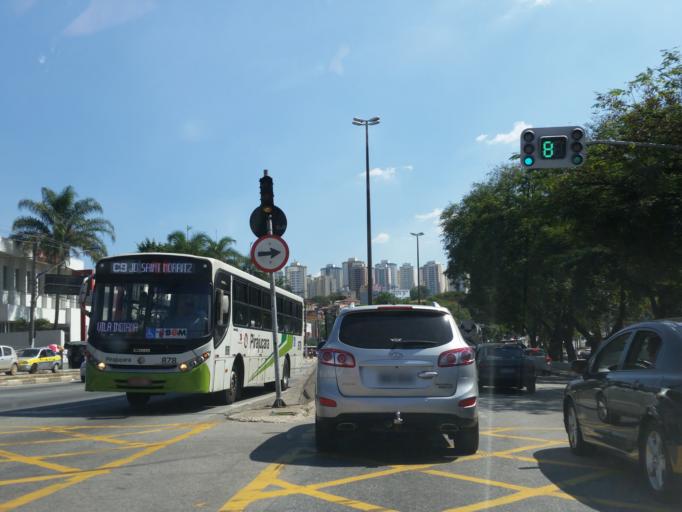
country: BR
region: Sao Paulo
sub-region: Taboao Da Serra
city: Taboao da Serra
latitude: -23.6088
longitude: -46.7556
